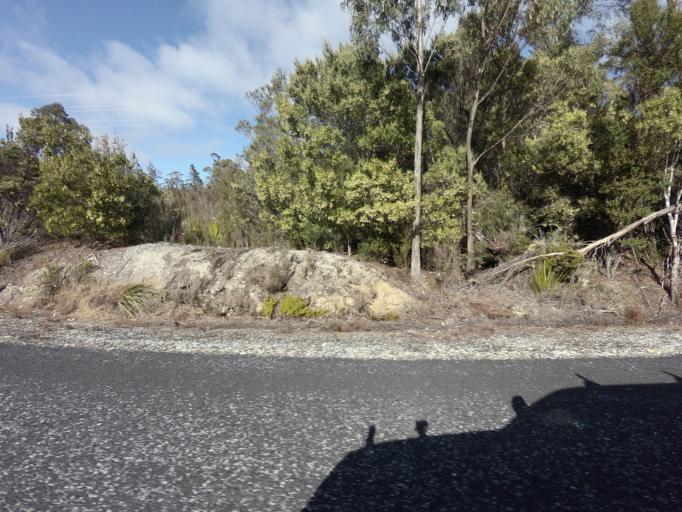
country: AU
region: Tasmania
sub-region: Huon Valley
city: Geeveston
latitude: -42.8157
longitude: 146.1040
